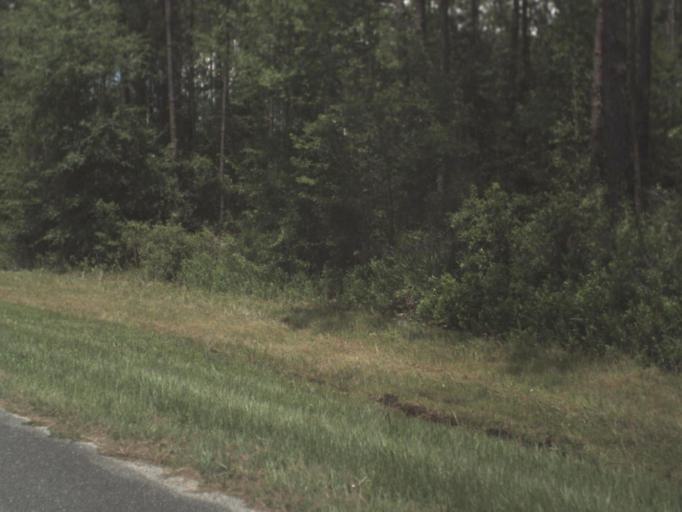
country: US
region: Florida
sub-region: Baker County
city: Macclenny
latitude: 30.3065
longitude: -82.1255
